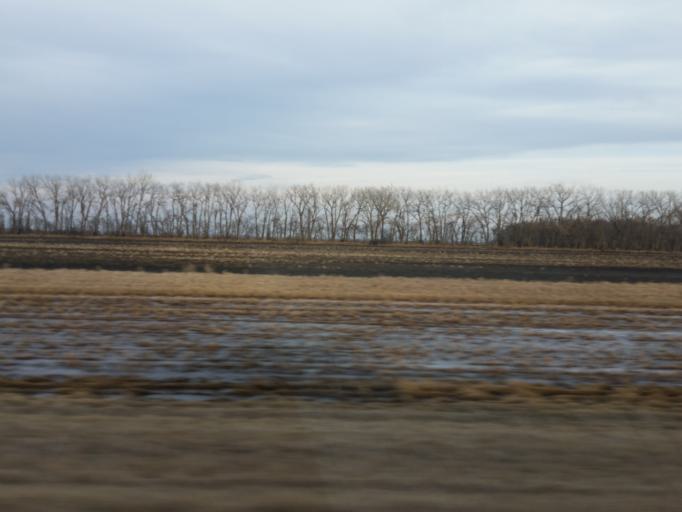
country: US
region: North Dakota
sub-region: Traill County
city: Hillsboro
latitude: 47.2765
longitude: -97.2175
